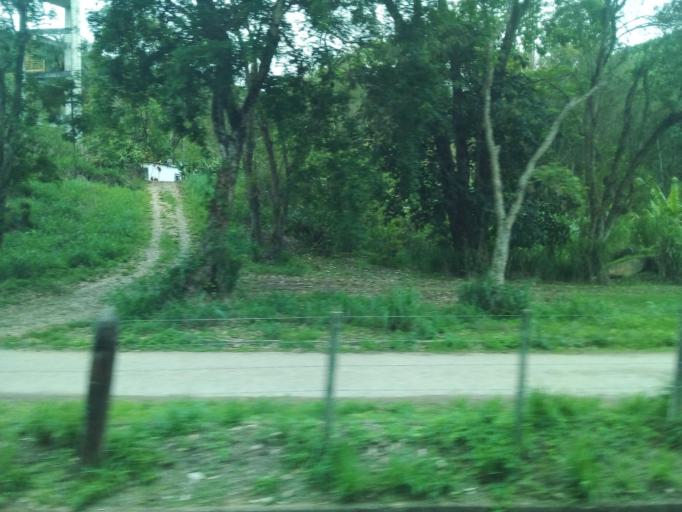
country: BR
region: Minas Gerais
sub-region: Nova Era
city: Nova Era
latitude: -19.7258
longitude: -42.9921
